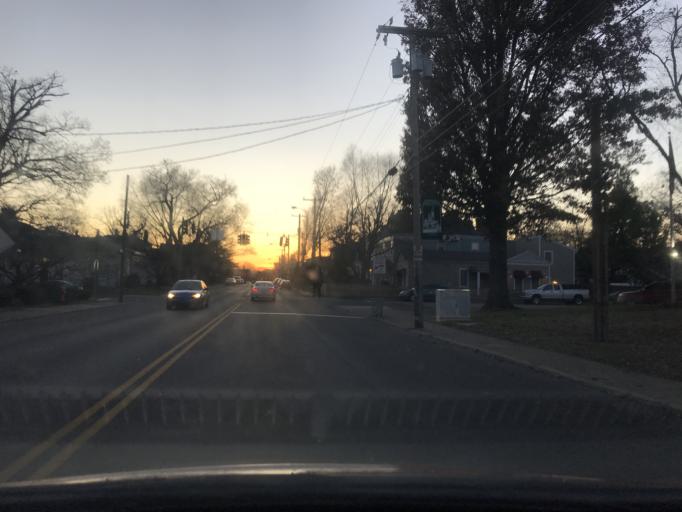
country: US
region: Kentucky
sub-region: Jefferson County
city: Audubon Park
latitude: 38.2376
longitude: -85.7239
